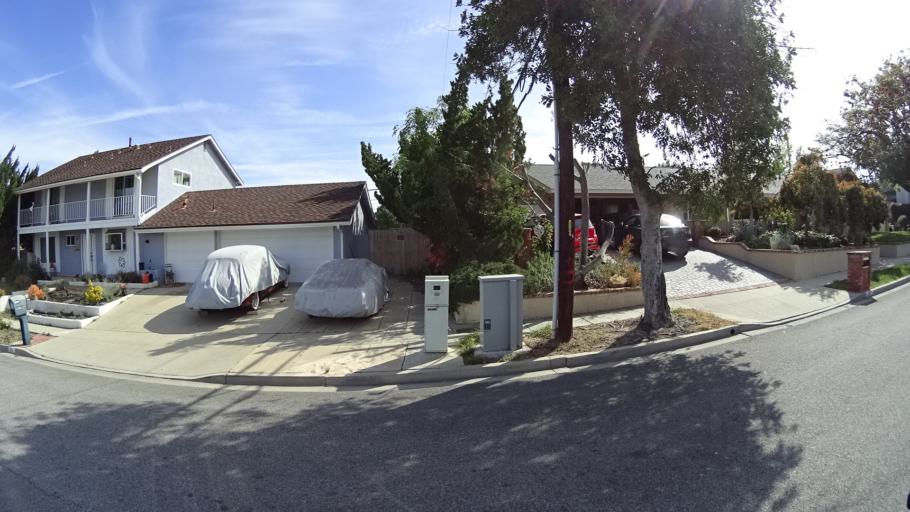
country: US
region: California
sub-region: Ventura County
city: Thousand Oaks
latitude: 34.2045
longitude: -118.8757
